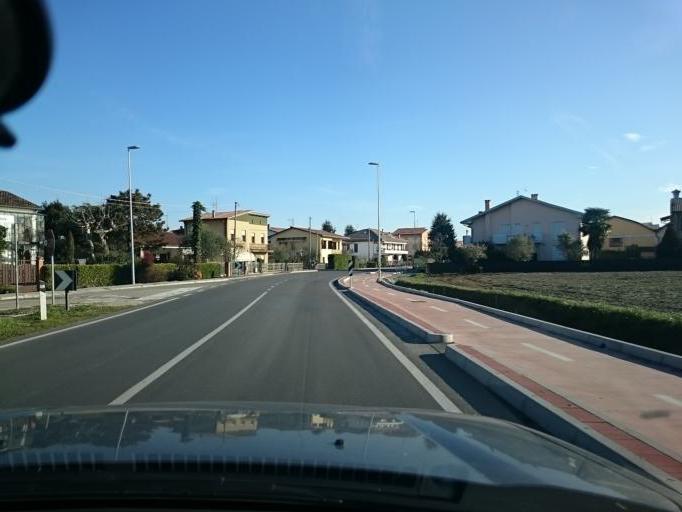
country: IT
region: Veneto
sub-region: Provincia di Padova
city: Masera di Padova
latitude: 45.3203
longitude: 11.8577
